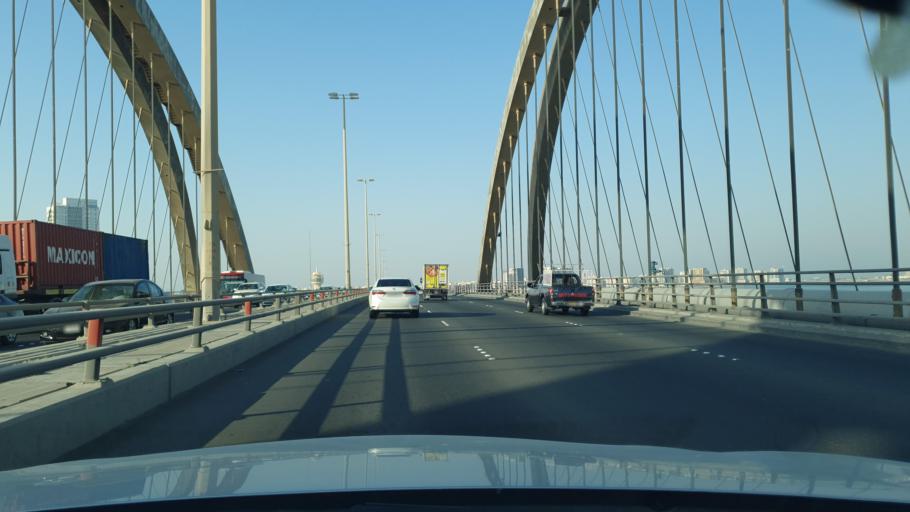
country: BH
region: Muharraq
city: Al Hadd
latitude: 26.2188
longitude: 50.6269
